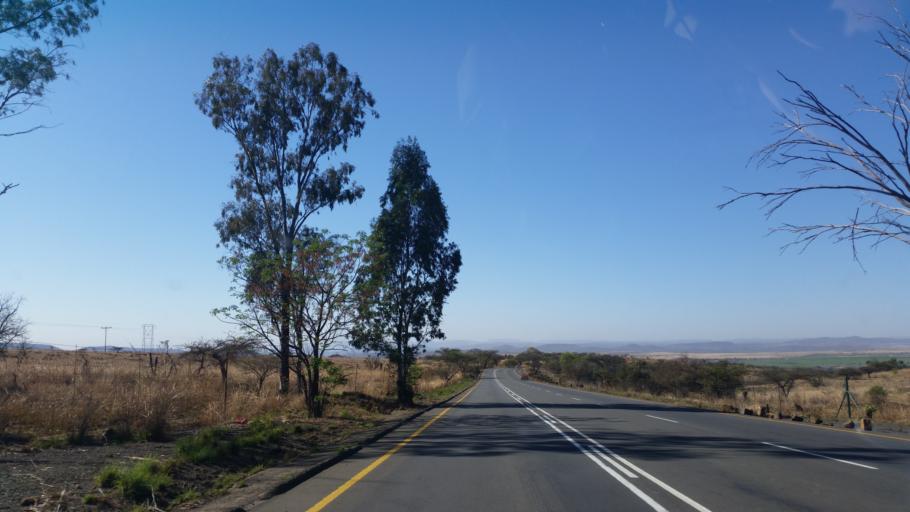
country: ZA
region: KwaZulu-Natal
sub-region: uThukela District Municipality
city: Ladysmith
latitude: -28.7004
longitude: 29.7747
